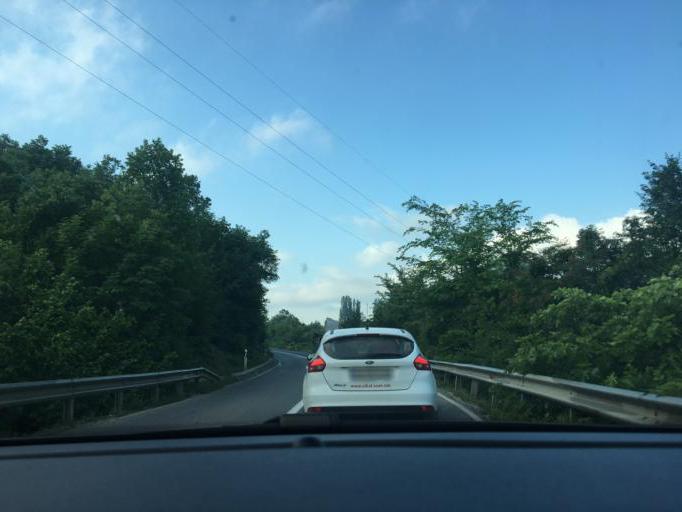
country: MK
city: Kuklish
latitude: 41.3734
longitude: 22.6045
